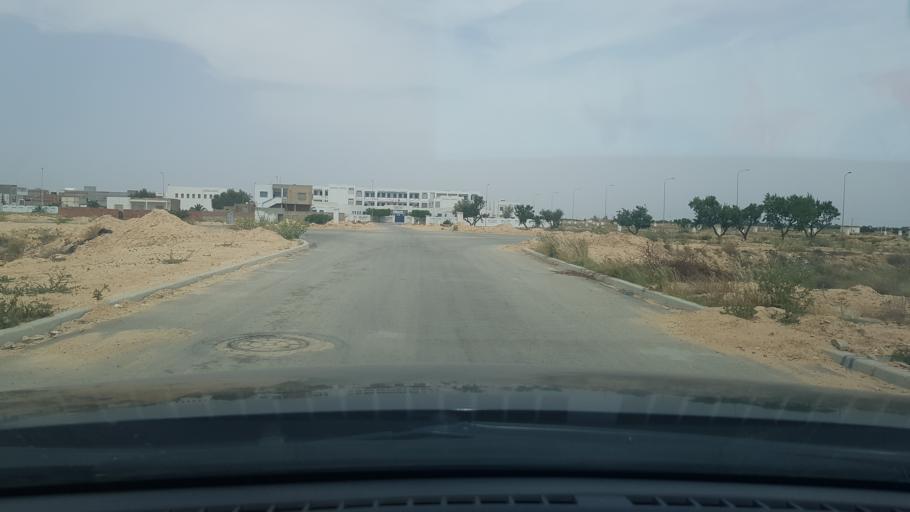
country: TN
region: Safaqis
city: Al Qarmadah
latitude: 34.8239
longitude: 10.7452
